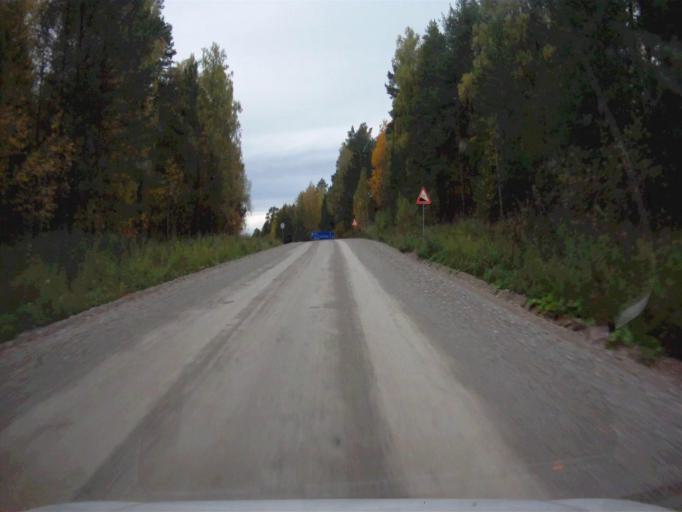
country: RU
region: Chelyabinsk
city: Nyazepetrovsk
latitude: 56.0853
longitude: 59.4194
